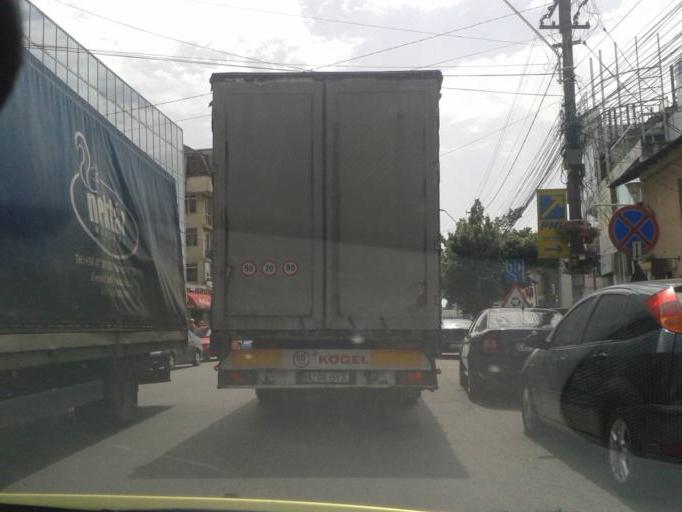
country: RO
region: Dambovita
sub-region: Oras Gaesti
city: Gaesti
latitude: 44.7195
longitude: 25.3217
